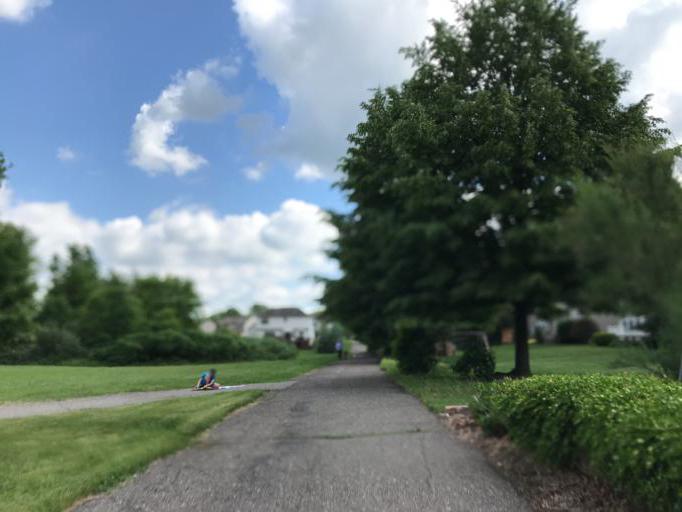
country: US
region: Michigan
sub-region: Oakland County
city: South Lyon
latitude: 42.4518
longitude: -83.6606
